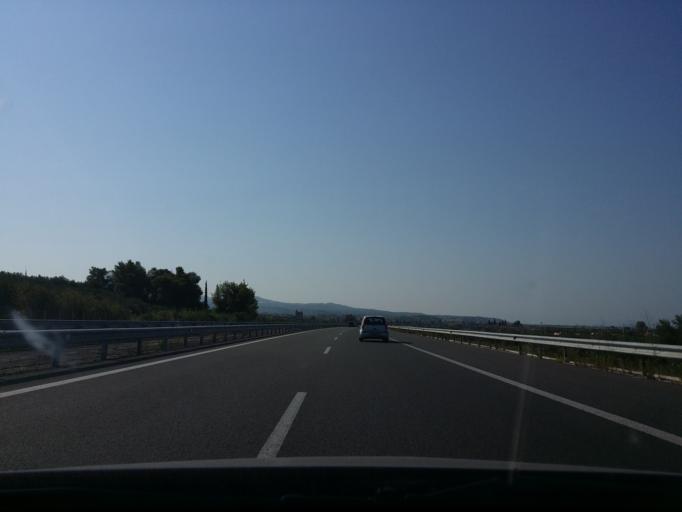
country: GR
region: Peloponnese
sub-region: Nomos Korinthias
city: Vokhaiko
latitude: 37.9418
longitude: 22.7646
